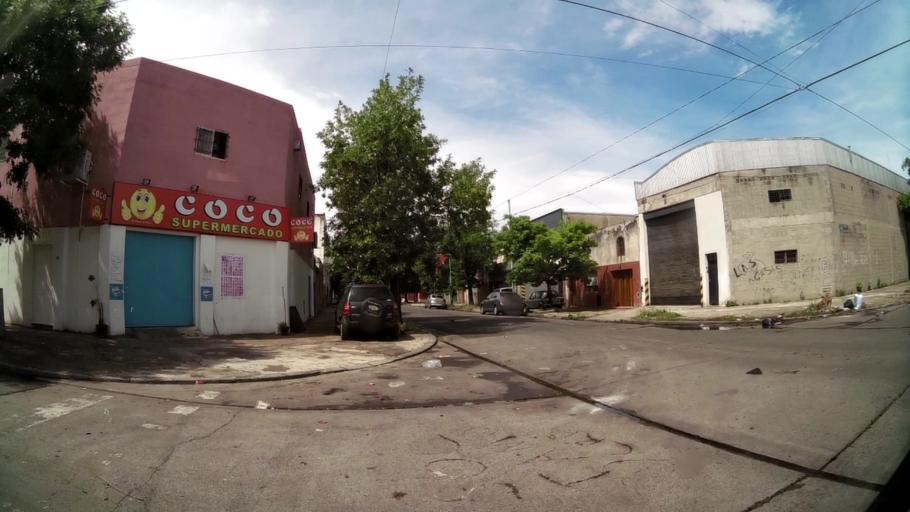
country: AR
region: Buenos Aires F.D.
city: Villa Lugano
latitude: -34.6605
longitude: -58.4267
